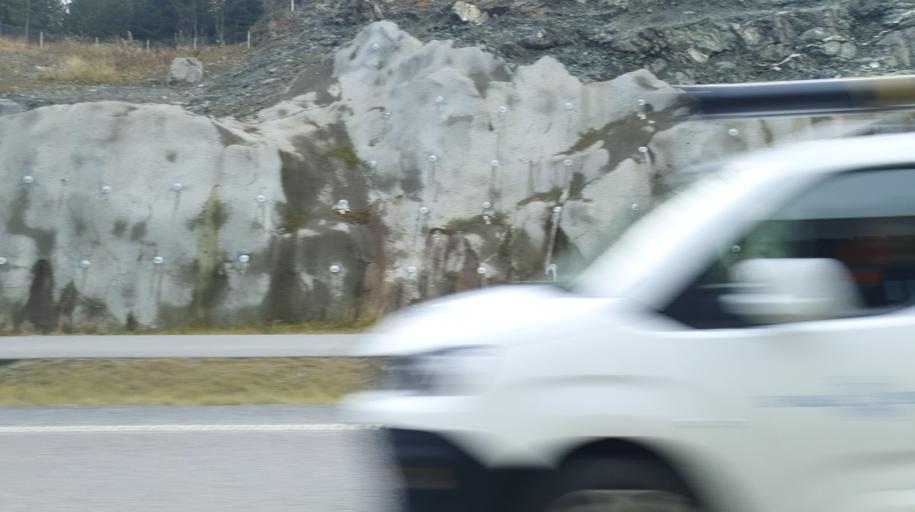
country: NO
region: Sor-Trondelag
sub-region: Klaebu
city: Klaebu
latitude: 63.3147
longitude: 10.4146
